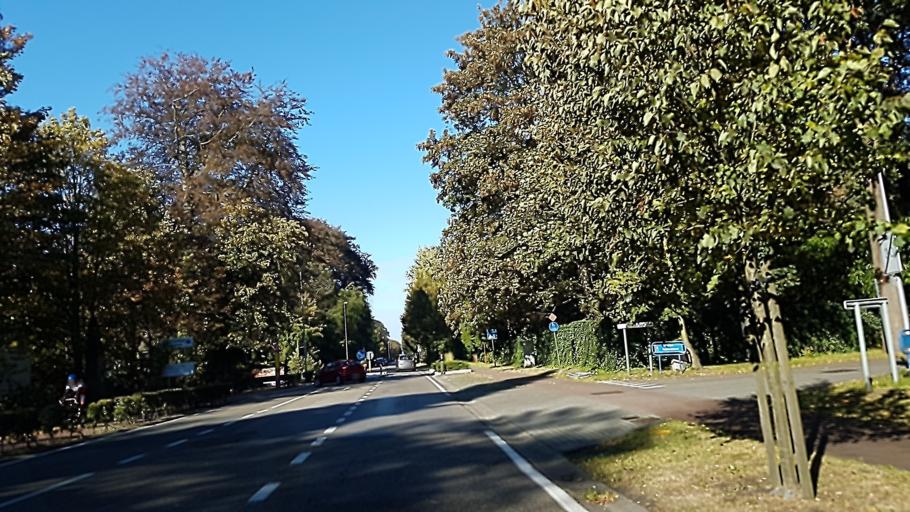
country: BE
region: Flanders
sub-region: Provincie Antwerpen
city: Kapellen
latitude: 51.3216
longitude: 4.4232
